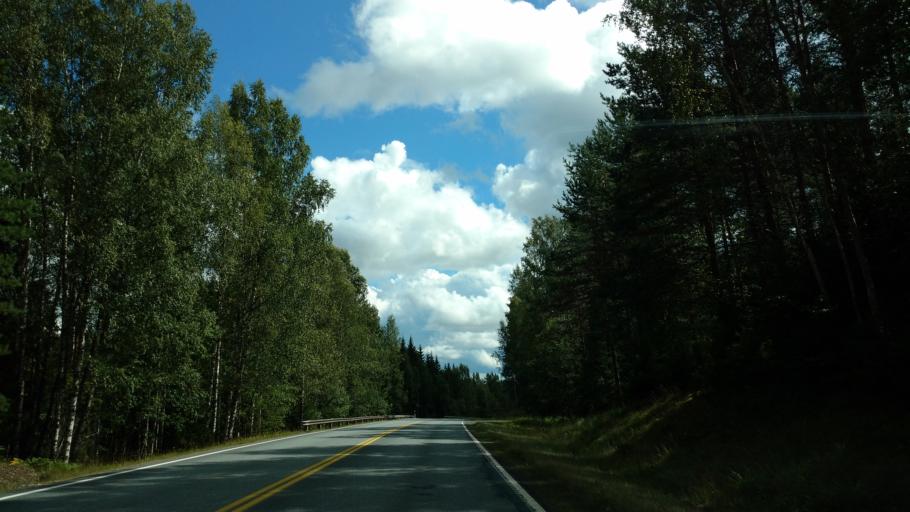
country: FI
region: Uusimaa
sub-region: Helsinki
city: Karjalohja
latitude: 60.2315
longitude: 23.6096
